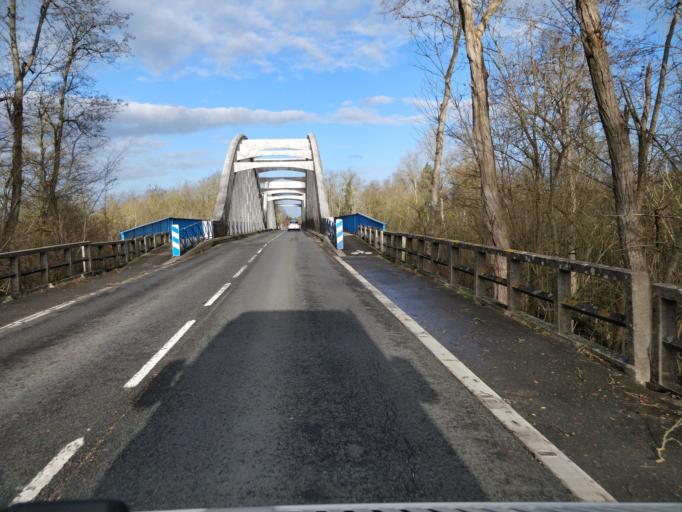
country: FR
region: Centre
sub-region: Departement du Loir-et-Cher
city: Muides-sur-Loire
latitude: 47.6764
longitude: 1.5255
